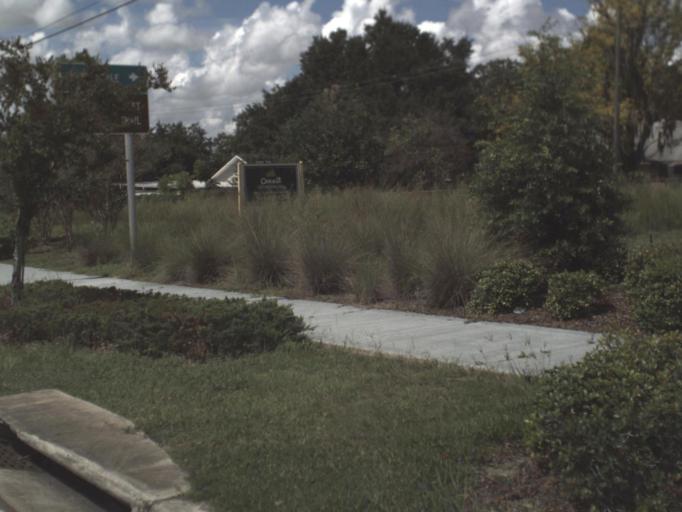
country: US
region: Florida
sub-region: Polk County
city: Polk City
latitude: 28.1809
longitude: -81.8248
